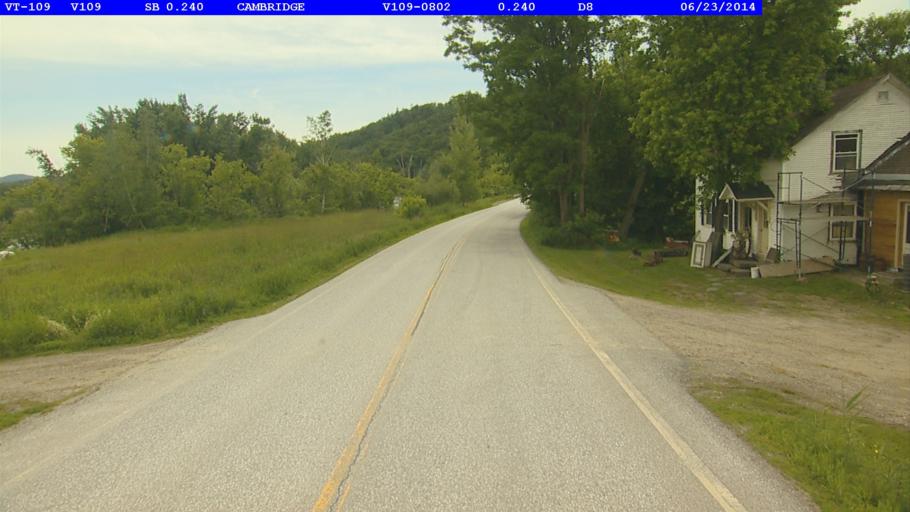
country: US
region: Vermont
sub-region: Lamoille County
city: Johnson
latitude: 44.6539
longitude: -72.8233
